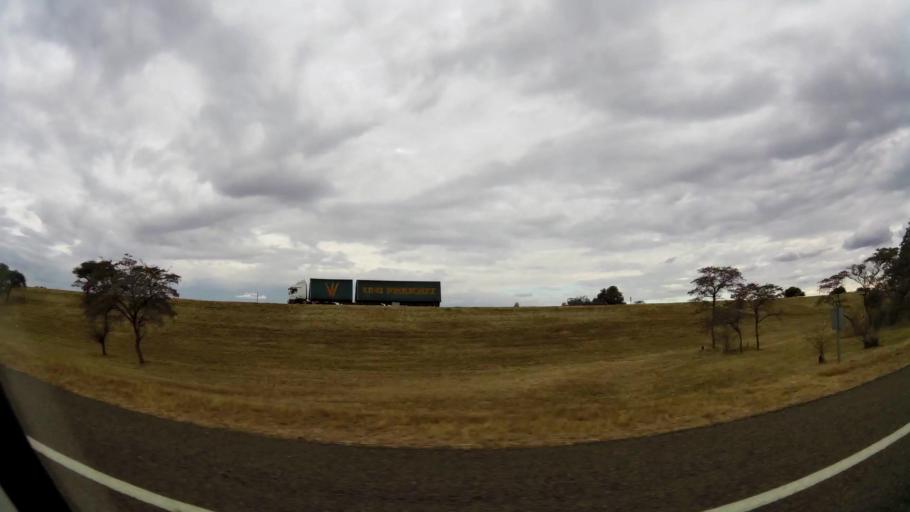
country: ZA
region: Limpopo
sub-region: Waterberg District Municipality
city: Modimolle
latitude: -24.6814
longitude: 28.5568
